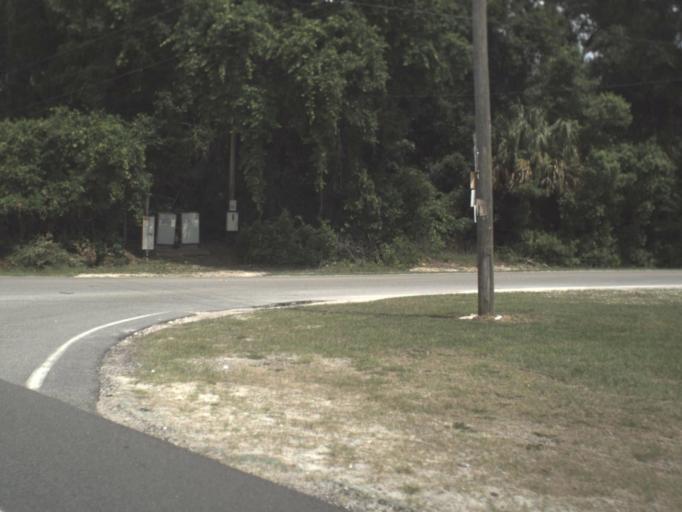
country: US
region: Florida
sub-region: Putnam County
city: Interlachen
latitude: 29.6145
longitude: -81.9784
